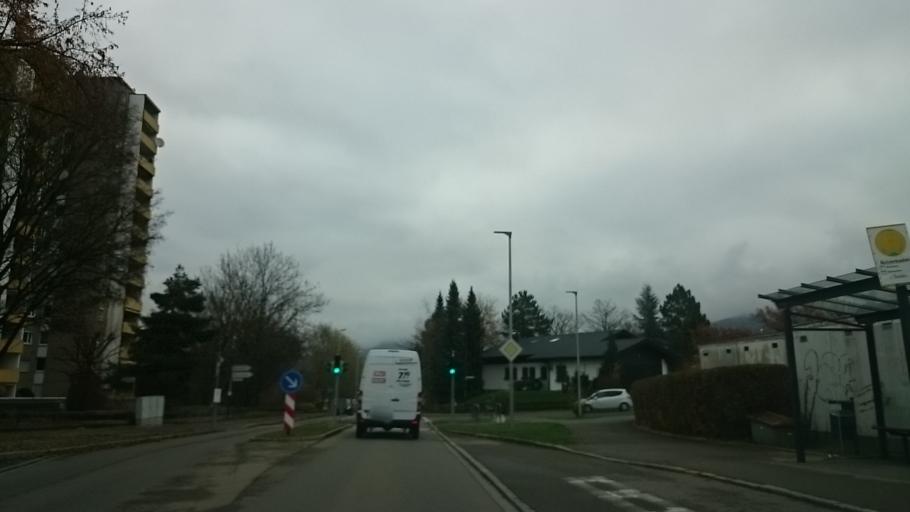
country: DE
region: Baden-Wuerttemberg
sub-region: Tuebingen Region
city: Ofterdingen
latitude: 48.4040
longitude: 9.0354
